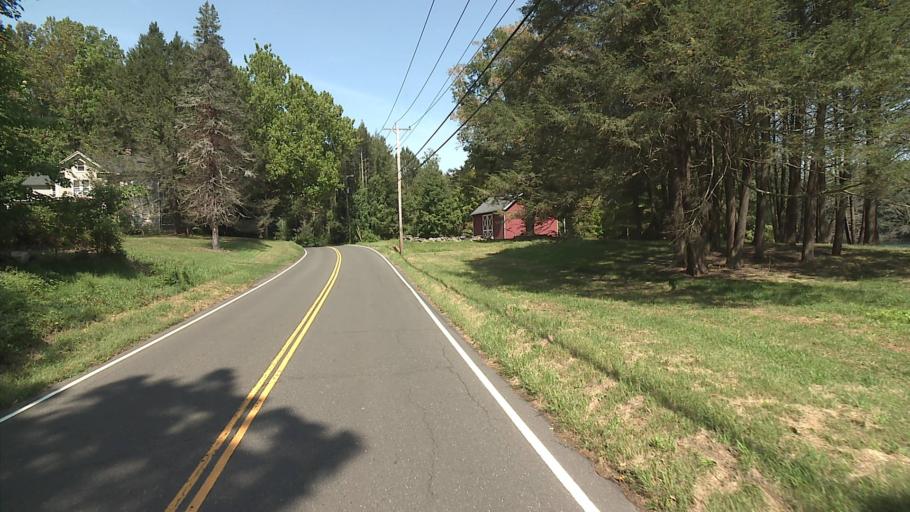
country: US
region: Connecticut
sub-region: Fairfield County
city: Westport
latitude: 41.2371
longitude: -73.3209
